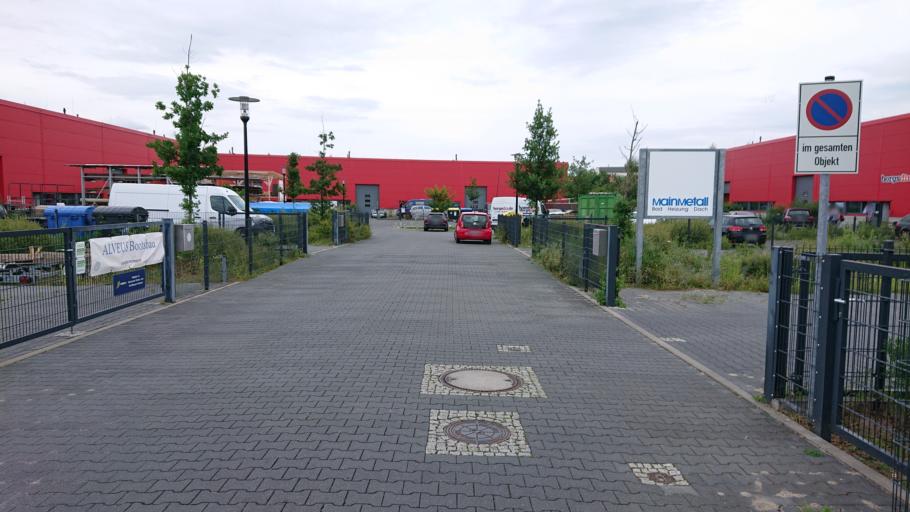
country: DE
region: Brandenburg
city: Potsdam
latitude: 52.3811
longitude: 13.1042
